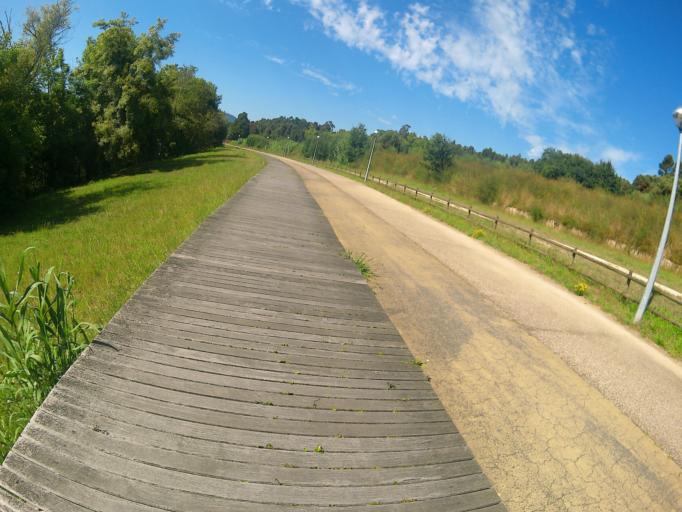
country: PT
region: Viana do Castelo
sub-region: Valenca
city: Valenca
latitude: 42.0212
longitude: -8.6562
